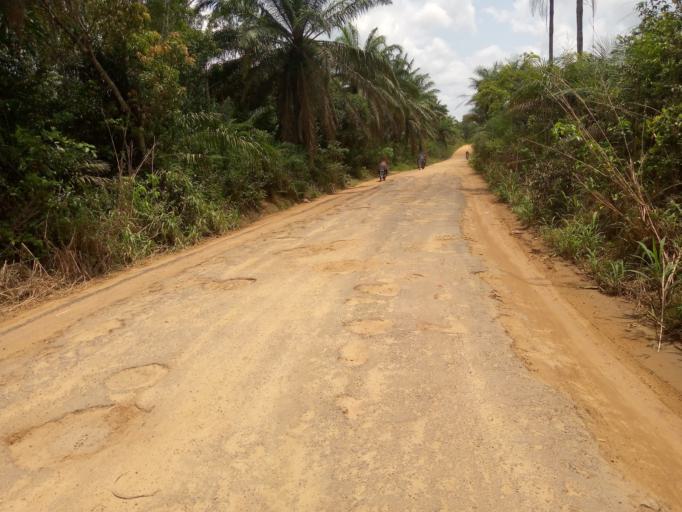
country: SL
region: Western Area
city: Waterloo
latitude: 8.3706
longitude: -12.9618
